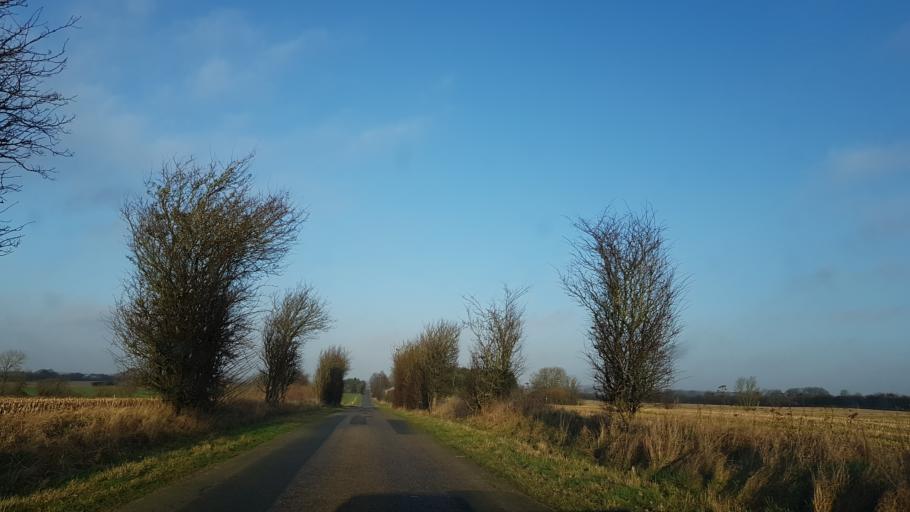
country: DK
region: South Denmark
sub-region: Aabenraa Kommune
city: Rodekro
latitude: 55.1441
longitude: 9.3144
